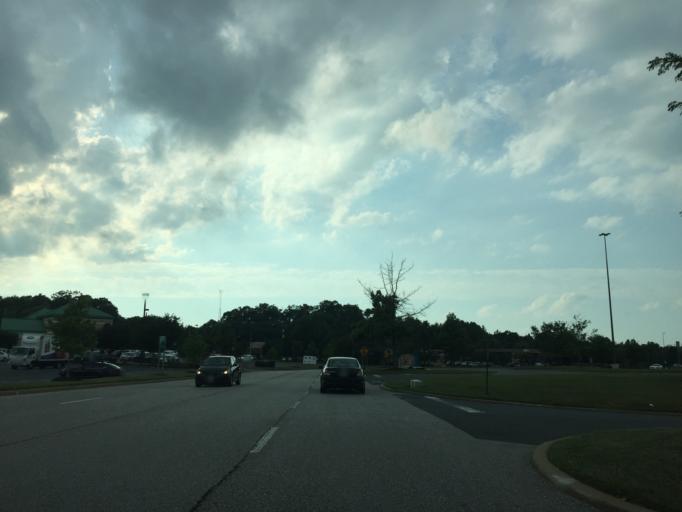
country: US
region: Maryland
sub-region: Baltimore County
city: Rossville
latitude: 39.3738
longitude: -76.4704
